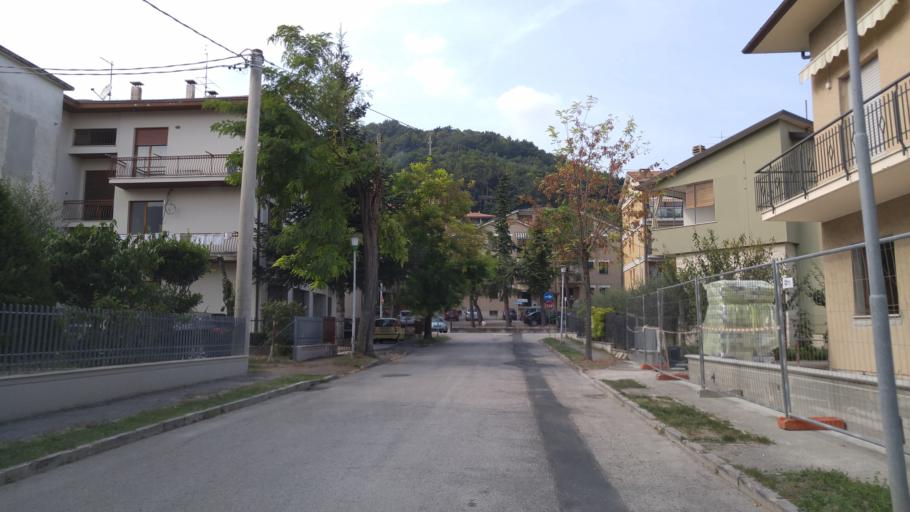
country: IT
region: The Marches
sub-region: Provincia di Pesaro e Urbino
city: Fossombrone
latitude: 43.6926
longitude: 12.8163
